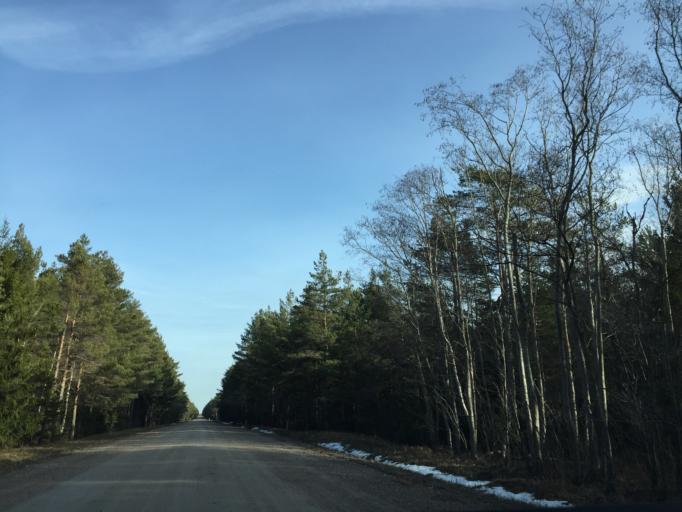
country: EE
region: Saare
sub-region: Kuressaare linn
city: Kuressaare
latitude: 58.3062
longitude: 21.9690
